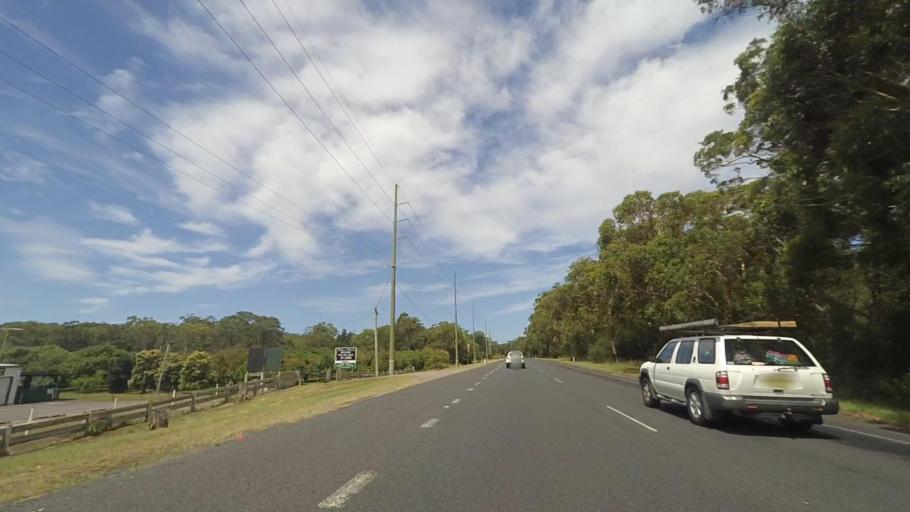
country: AU
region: New South Wales
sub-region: Port Stephens Shire
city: Anna Bay
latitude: -32.7844
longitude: 151.9743
